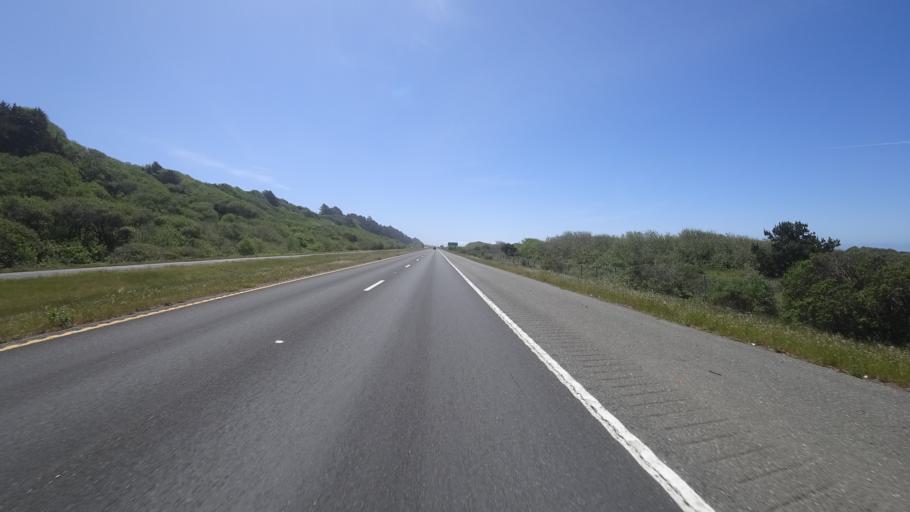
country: US
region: California
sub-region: Humboldt County
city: McKinleyville
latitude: 40.9892
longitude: -124.1155
